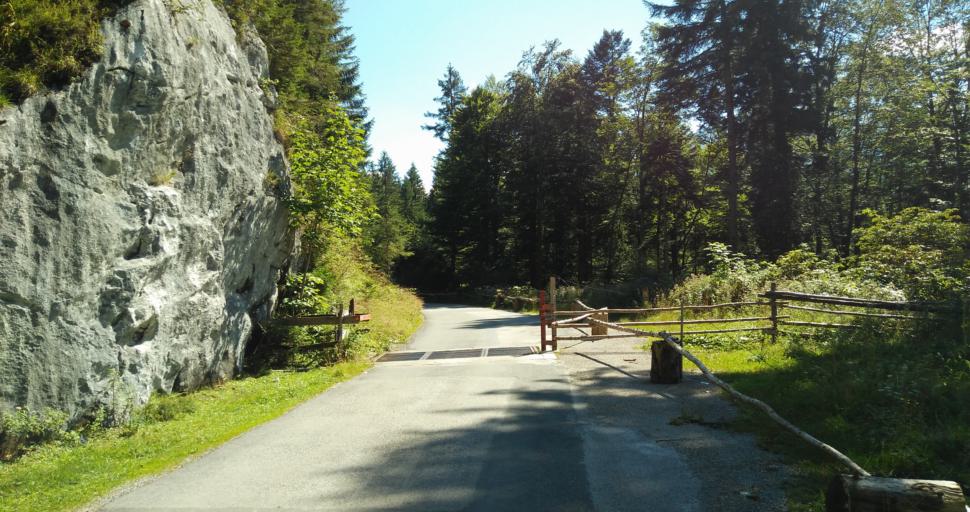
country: AT
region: Salzburg
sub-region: Politischer Bezirk Hallein
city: Scheffau am Tennengebirge
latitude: 47.6298
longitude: 13.2412
